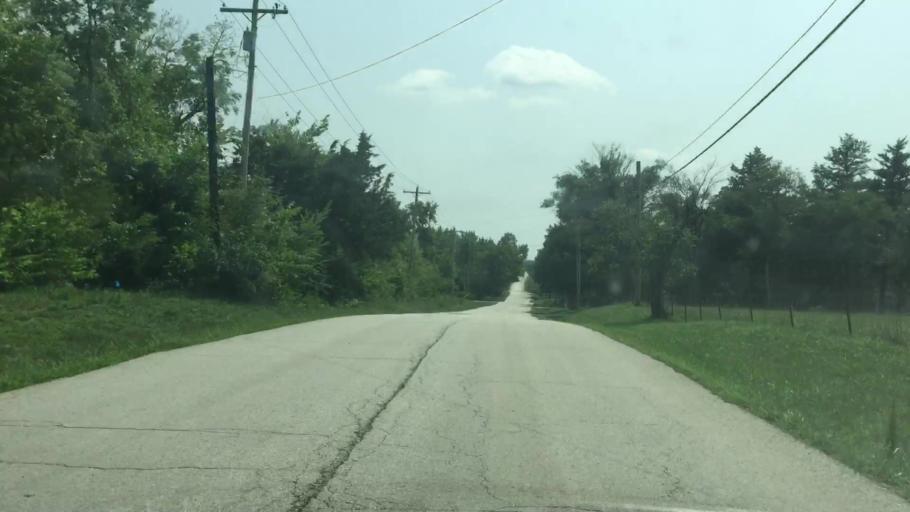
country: US
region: Kansas
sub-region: Douglas County
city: Baldwin City
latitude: 38.7746
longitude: -95.2049
